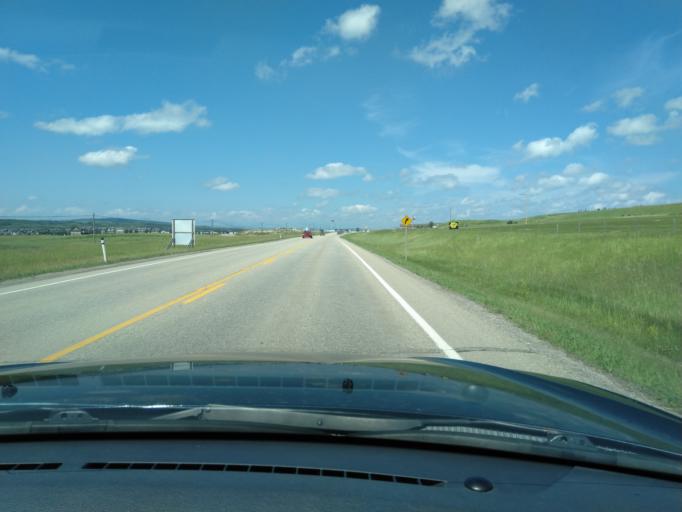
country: CA
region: Alberta
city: Cochrane
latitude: 51.2008
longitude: -114.4928
